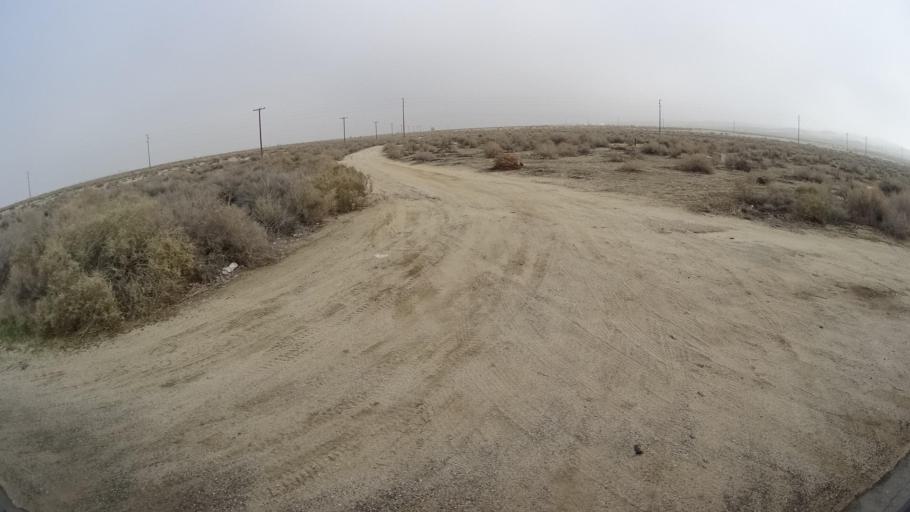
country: US
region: California
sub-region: Kern County
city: Ford City
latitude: 35.1859
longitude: -119.4290
